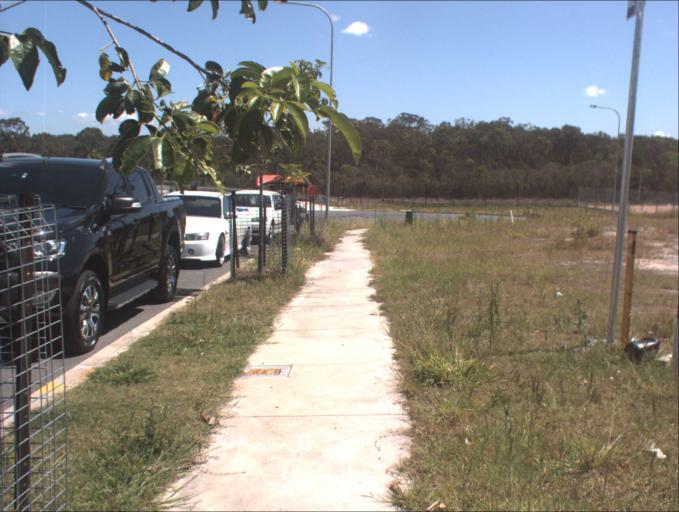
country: AU
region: Queensland
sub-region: Logan
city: Woodridge
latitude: -27.6487
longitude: 153.0909
